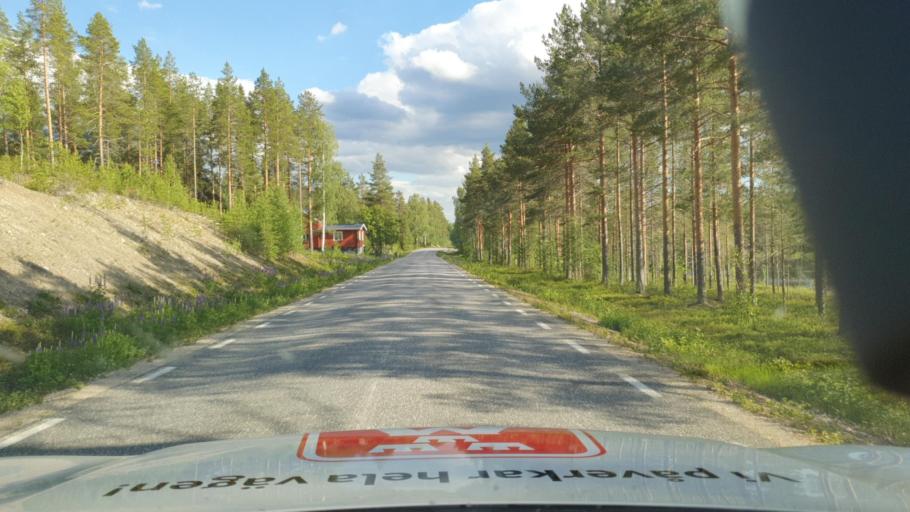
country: SE
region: Vaesterbotten
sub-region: Vindelns Kommun
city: Vindeln
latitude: 64.5011
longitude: 19.7987
